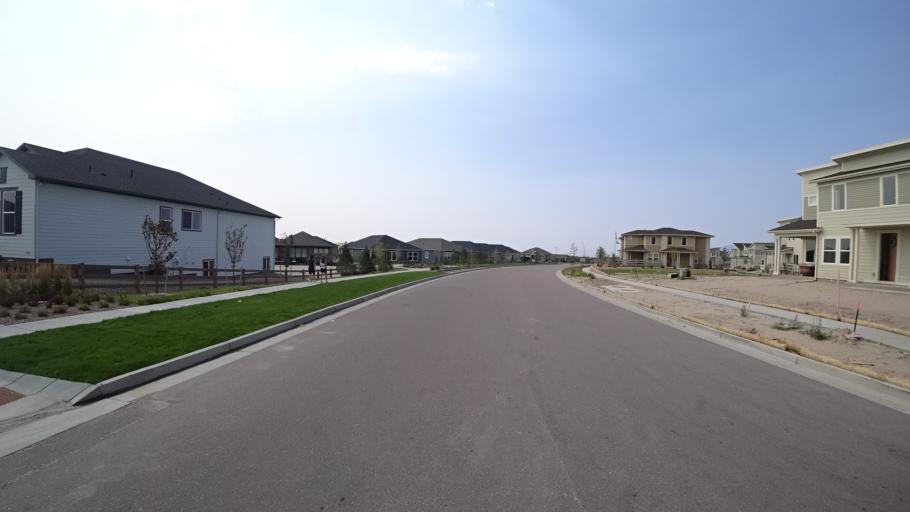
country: US
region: Colorado
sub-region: El Paso County
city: Black Forest
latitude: 38.9736
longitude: -104.7151
